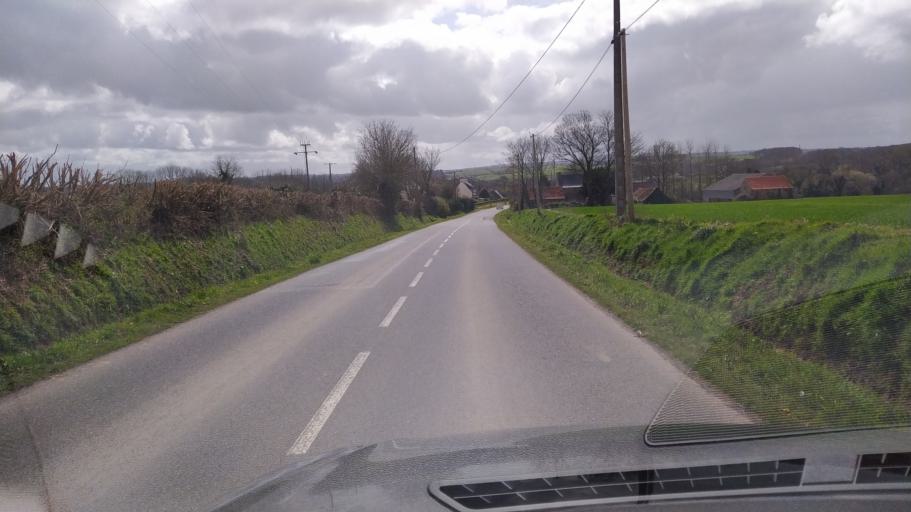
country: FR
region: Brittany
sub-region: Departement du Finistere
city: Bodilis
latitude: 48.5207
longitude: -4.1234
